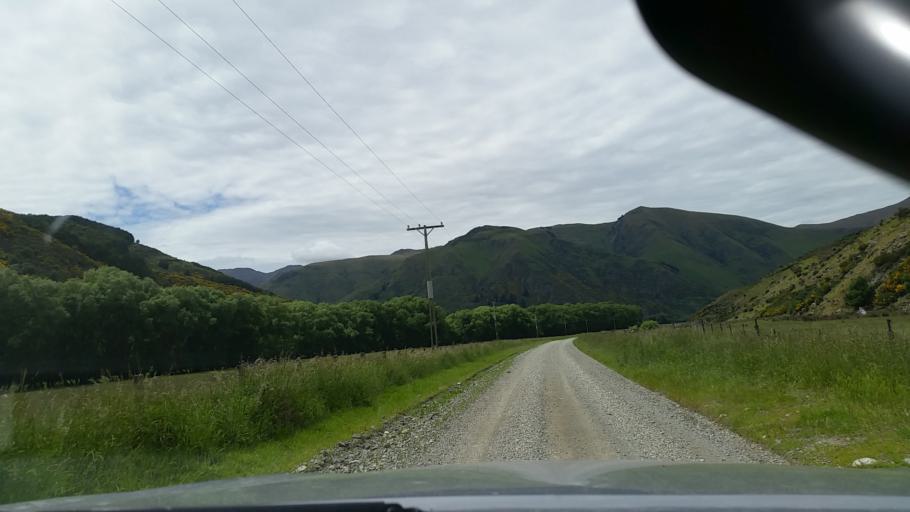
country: NZ
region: Otago
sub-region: Queenstown-Lakes District
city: Kingston
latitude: -45.5553
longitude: 168.6248
